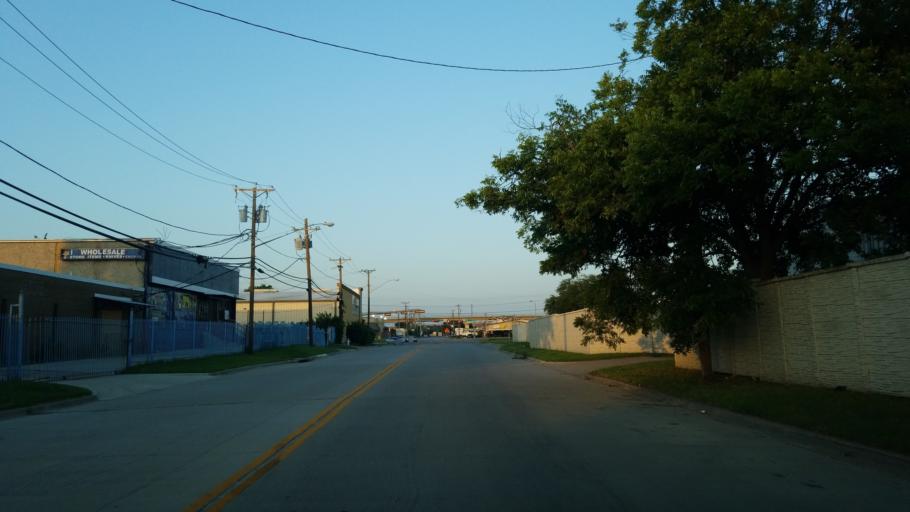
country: US
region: Texas
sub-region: Dallas County
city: Farmers Branch
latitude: 32.8864
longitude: -96.8895
